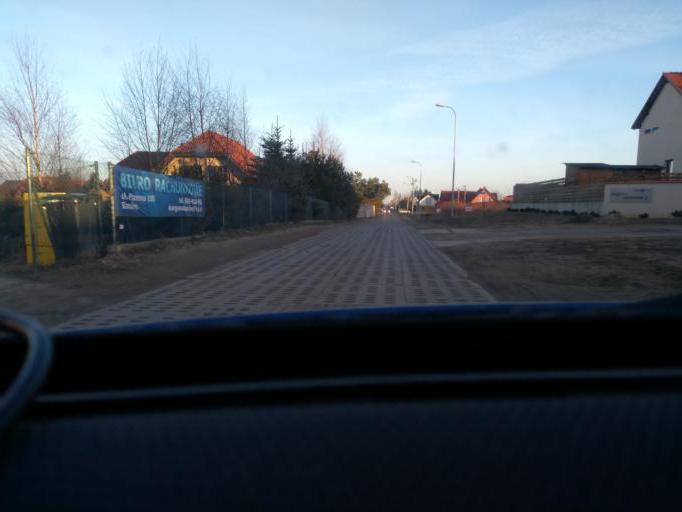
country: PL
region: Pomeranian Voivodeship
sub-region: Powiat kartuski
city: Banino
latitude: 54.3855
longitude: 18.3873
